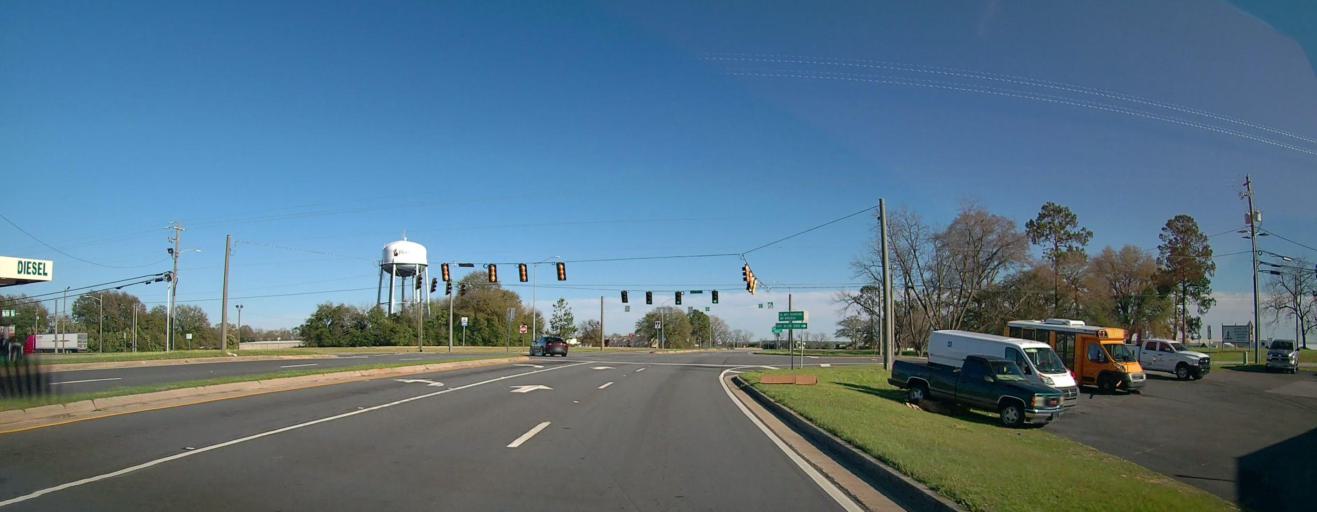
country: US
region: Georgia
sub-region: Houston County
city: Perry
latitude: 32.4459
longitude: -83.7516
